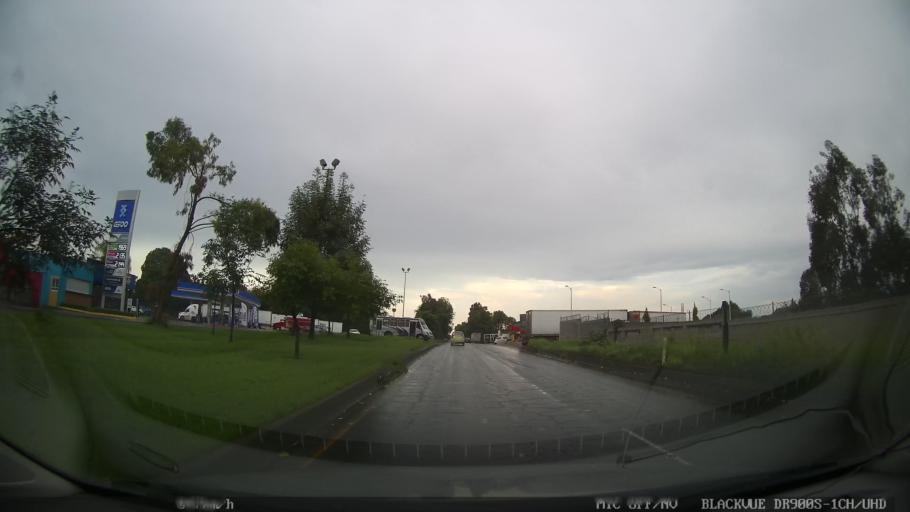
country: MX
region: Michoacan
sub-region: Uruapan
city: Santa Rosa (Santa Barbara)
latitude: 19.3968
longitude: -102.0356
